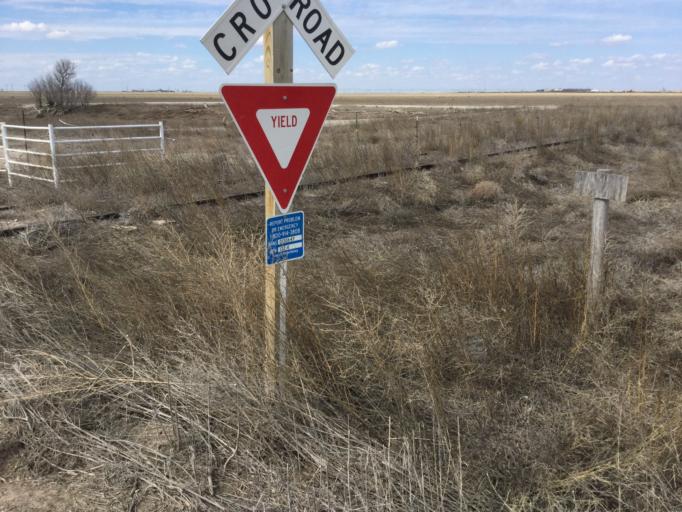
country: US
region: Kansas
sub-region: Scott County
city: Scott City
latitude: 38.3085
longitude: -100.9144
